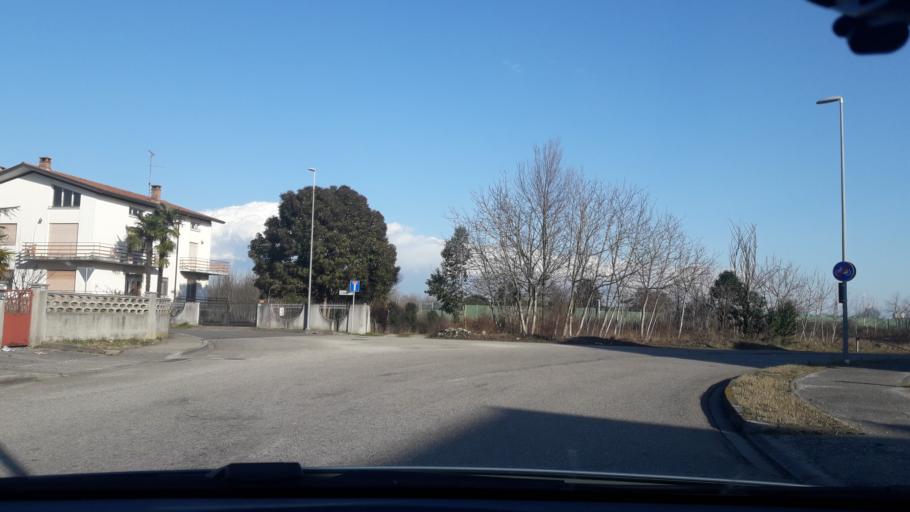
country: IT
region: Friuli Venezia Giulia
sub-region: Provincia di Udine
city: Passons
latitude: 46.0668
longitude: 13.1947
